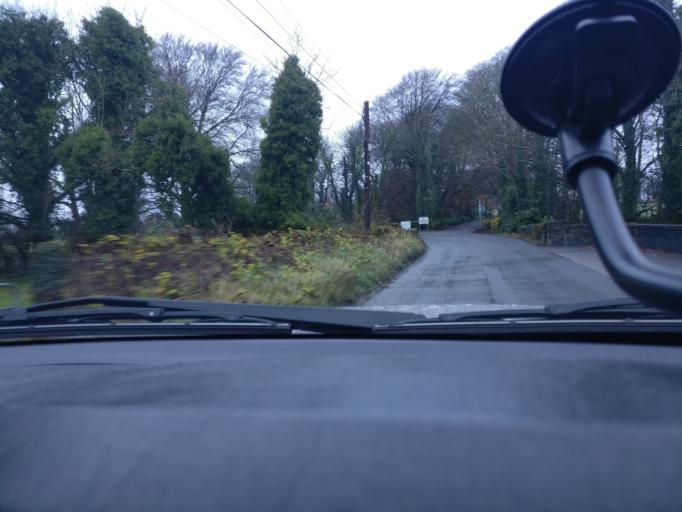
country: IE
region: Connaught
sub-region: County Galway
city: Loughrea
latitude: 53.2501
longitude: -8.5593
